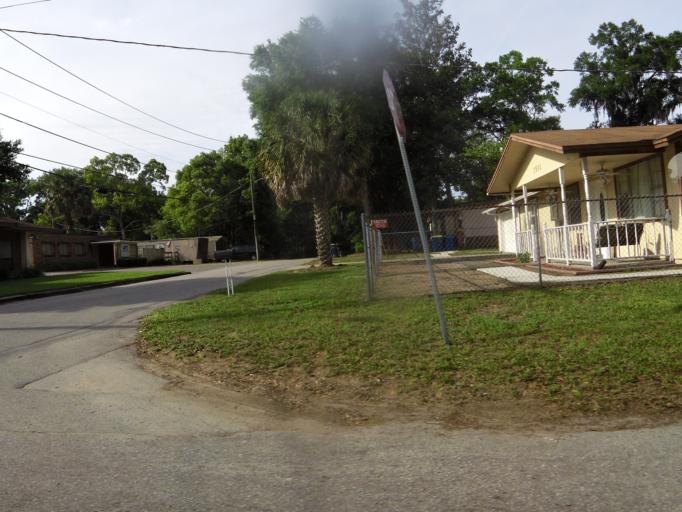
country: US
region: Florida
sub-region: Duval County
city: Jacksonville
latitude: 30.3359
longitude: -81.5994
